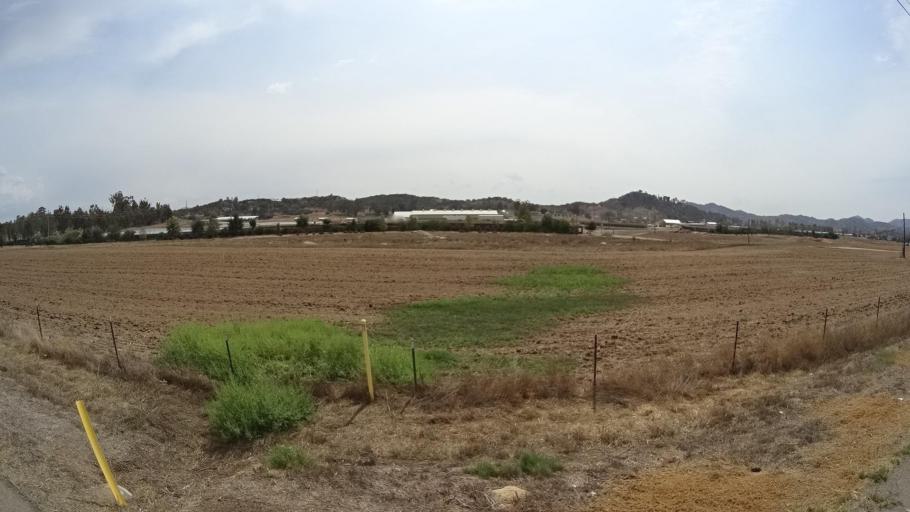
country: US
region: California
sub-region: San Diego County
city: Ramona
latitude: 33.0149
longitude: -116.8739
